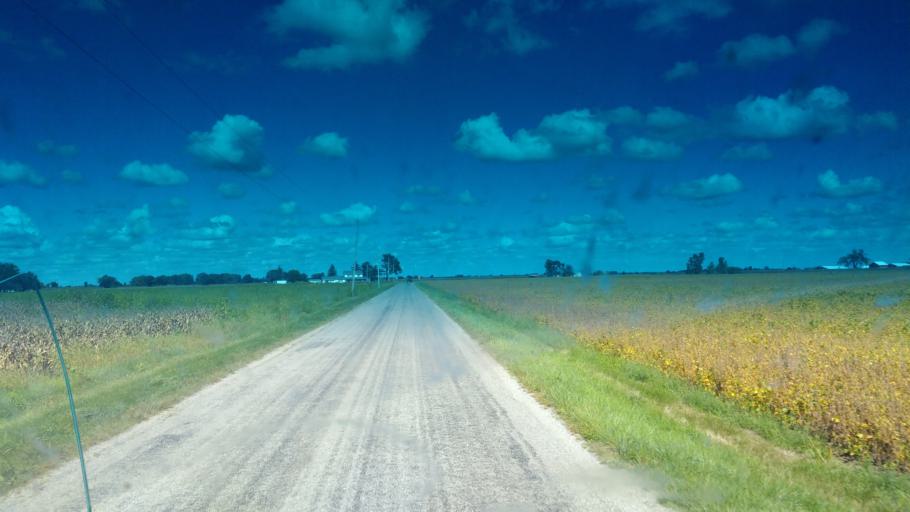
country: US
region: Ohio
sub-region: Madison County
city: Plain City
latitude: 40.0849
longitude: -83.3669
